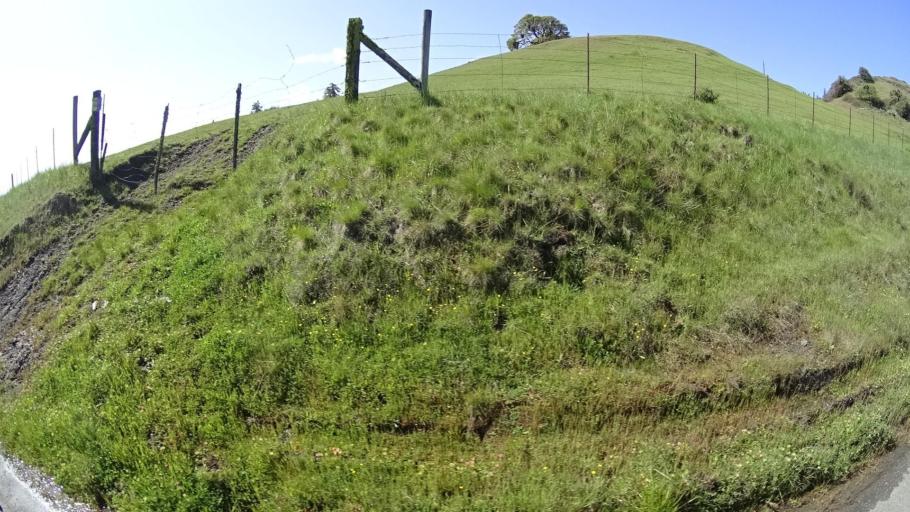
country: US
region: California
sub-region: Humboldt County
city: Redway
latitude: 40.0807
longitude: -123.6548
